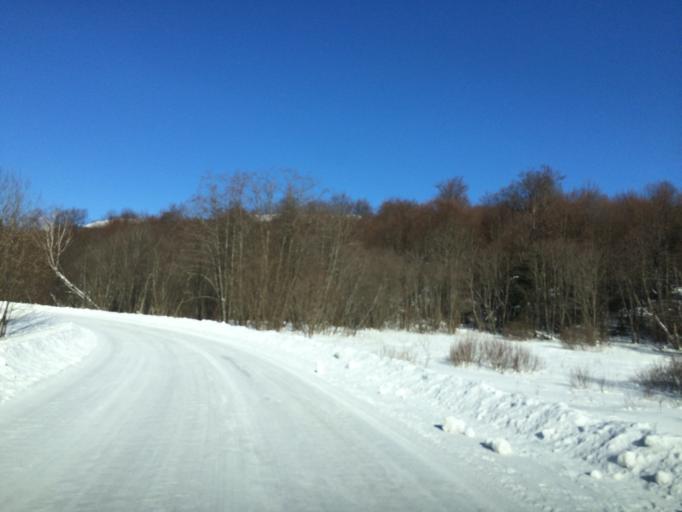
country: PL
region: Subcarpathian Voivodeship
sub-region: Powiat bieszczadzki
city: Lutowiska
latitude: 49.1069
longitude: 22.6288
